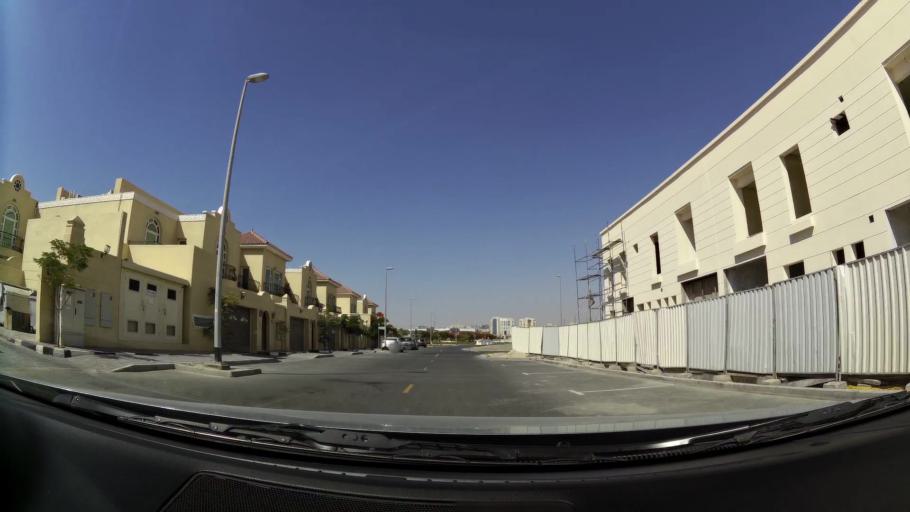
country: AE
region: Dubai
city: Dubai
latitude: 25.1060
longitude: 55.1868
